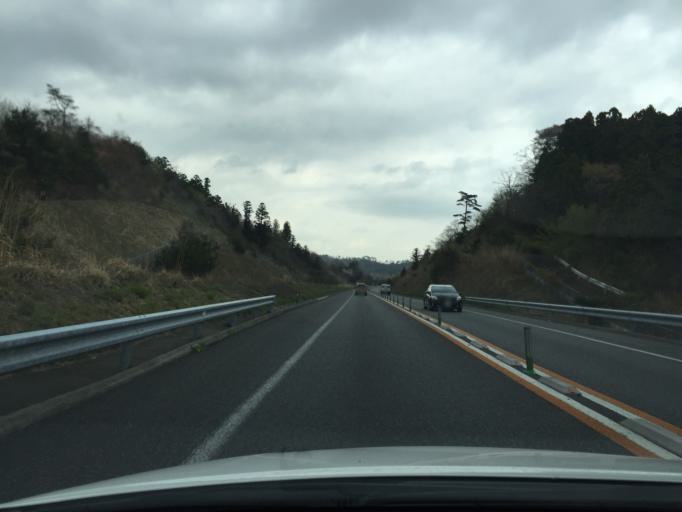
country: JP
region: Fukushima
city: Iwaki
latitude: 37.1607
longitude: 140.9665
